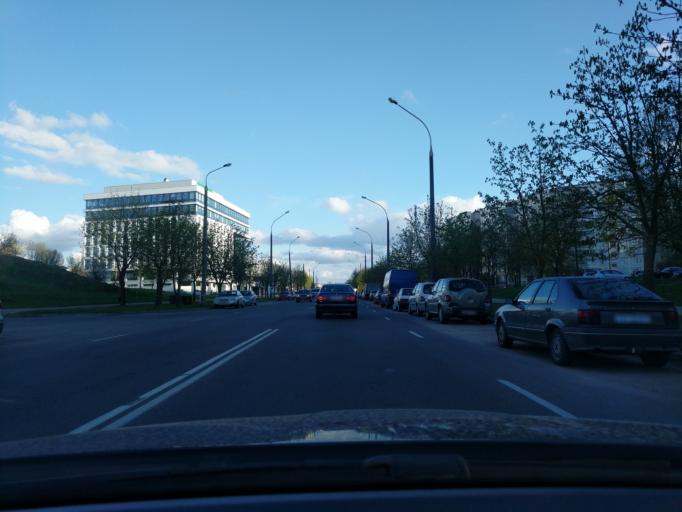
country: BY
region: Minsk
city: Novoye Medvezhino
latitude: 53.9106
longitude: 27.4517
